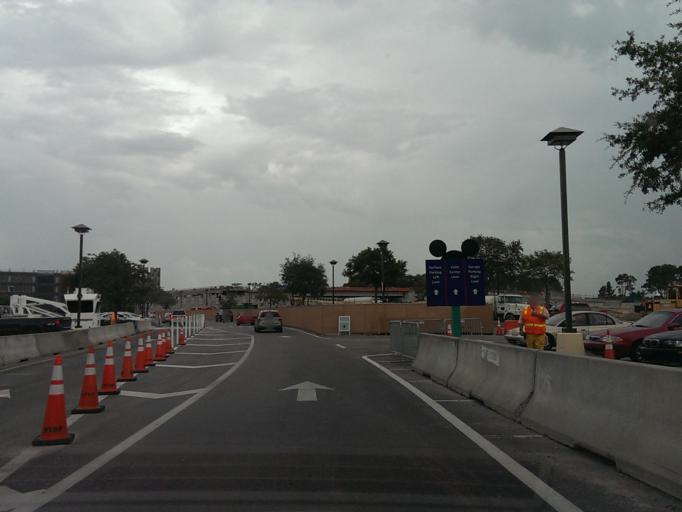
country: US
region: Florida
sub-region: Osceola County
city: Celebration
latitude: 28.3705
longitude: -81.5245
